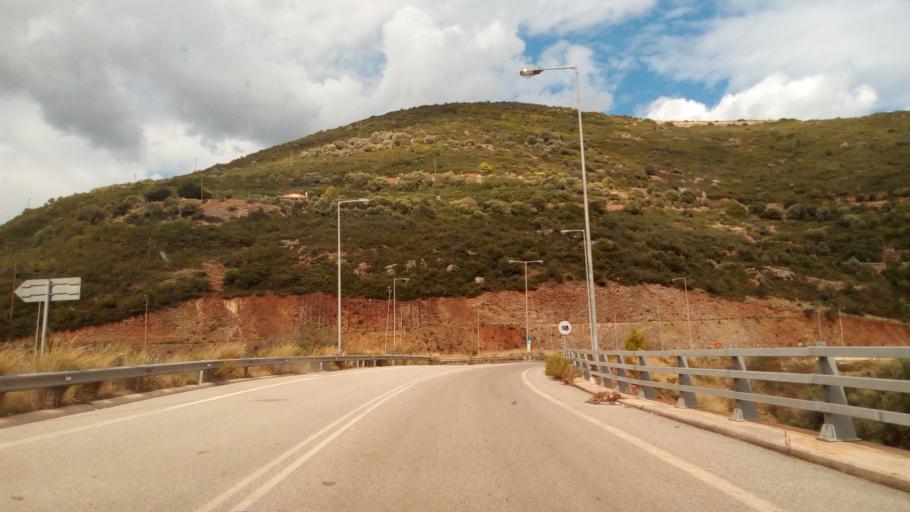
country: GR
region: West Greece
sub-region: Nomos Aitolias kai Akarnanias
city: Nafpaktos
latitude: 38.4127
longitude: 21.8427
